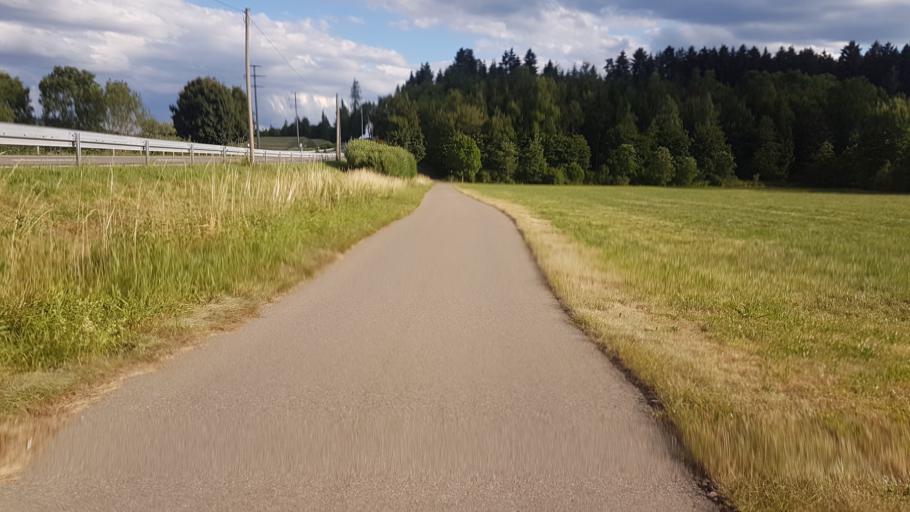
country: DE
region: Baden-Wuerttemberg
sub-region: Freiburg Region
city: Unterkirnach
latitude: 48.0102
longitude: 8.4086
